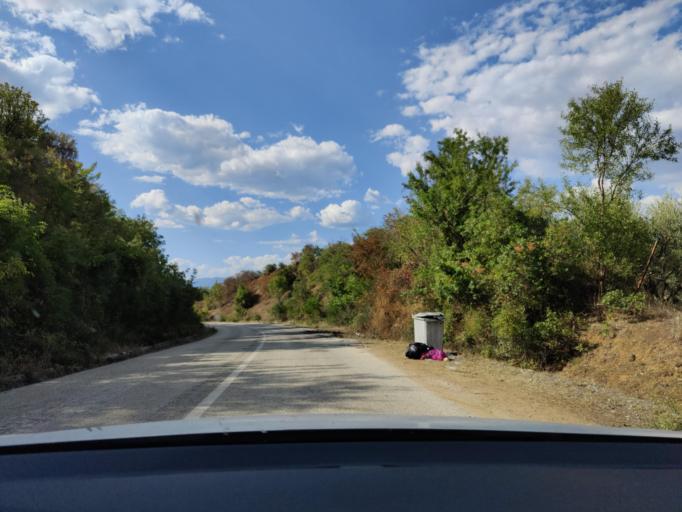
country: GR
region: Central Macedonia
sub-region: Nomos Serron
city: Chrysochorafa
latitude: 41.1486
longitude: 23.2078
